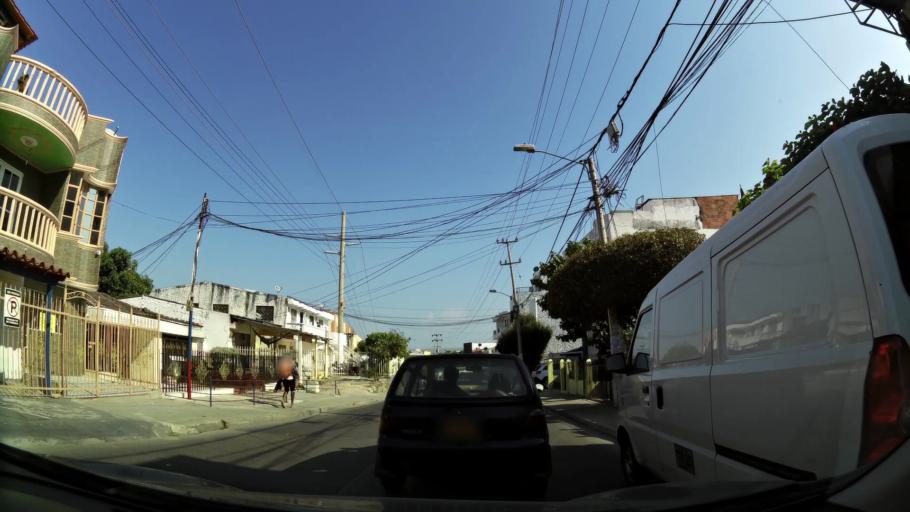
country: CO
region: Bolivar
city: Cartagena
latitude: 10.3971
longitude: -75.4961
